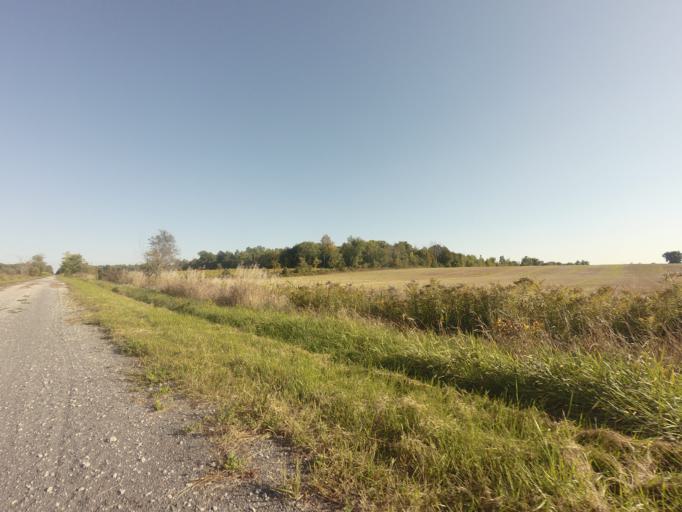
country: CA
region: Ontario
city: Hawkesbury
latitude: 45.5318
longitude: -74.5767
